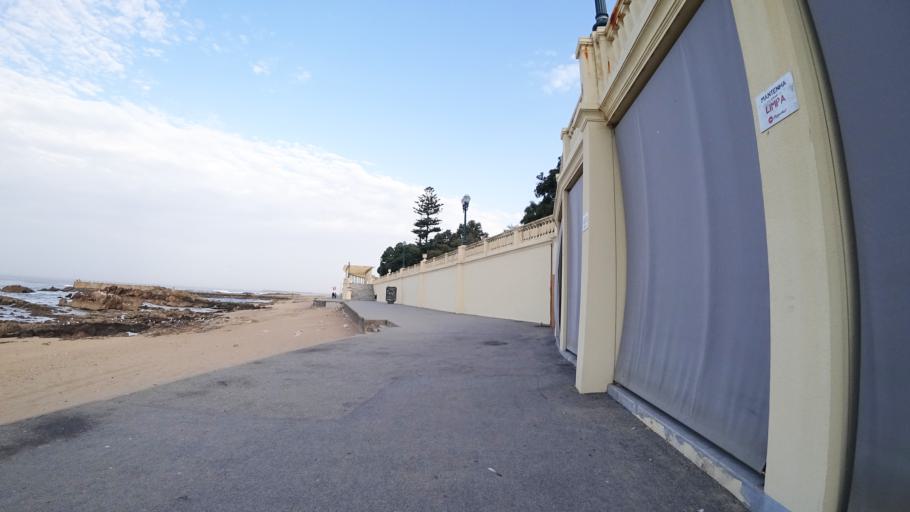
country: PT
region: Porto
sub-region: Matosinhos
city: Matosinhos
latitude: 41.1569
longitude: -8.6821
